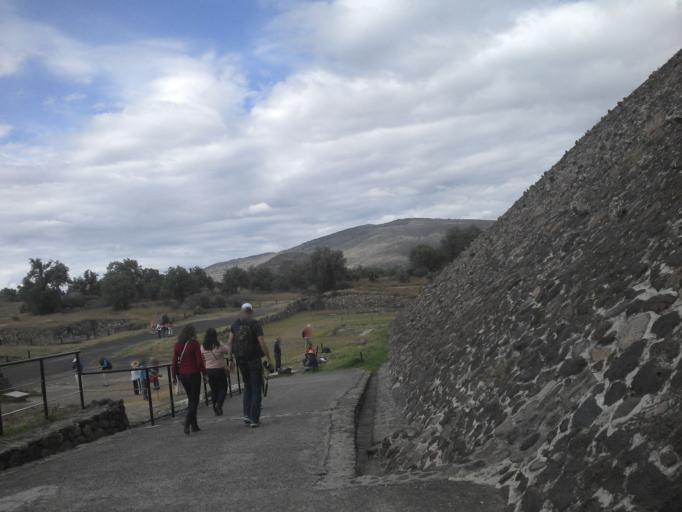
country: MX
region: Morelos
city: San Martin de las Piramides
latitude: 19.6930
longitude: -98.8445
